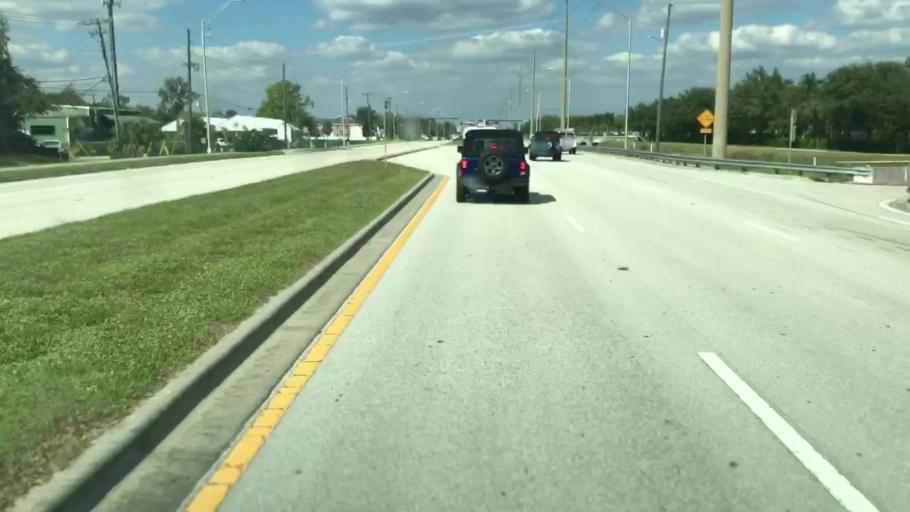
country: US
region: Florida
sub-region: Collier County
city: Vineyards
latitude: 26.2560
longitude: -81.6886
